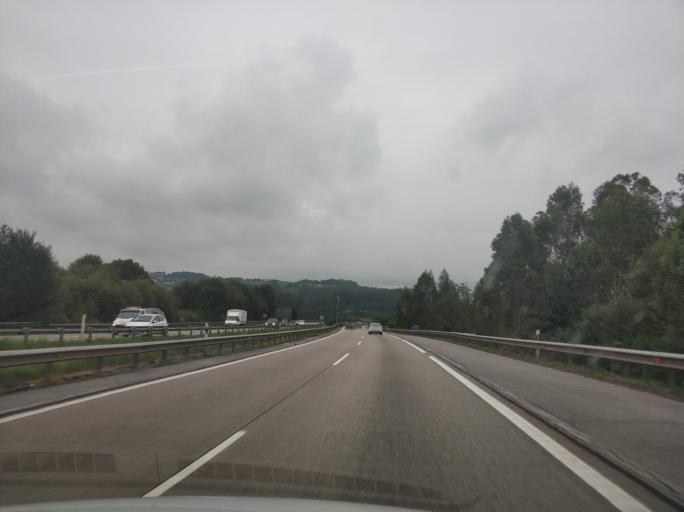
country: ES
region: Asturias
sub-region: Province of Asturias
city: Lugones
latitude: 43.4710
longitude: -5.7899
